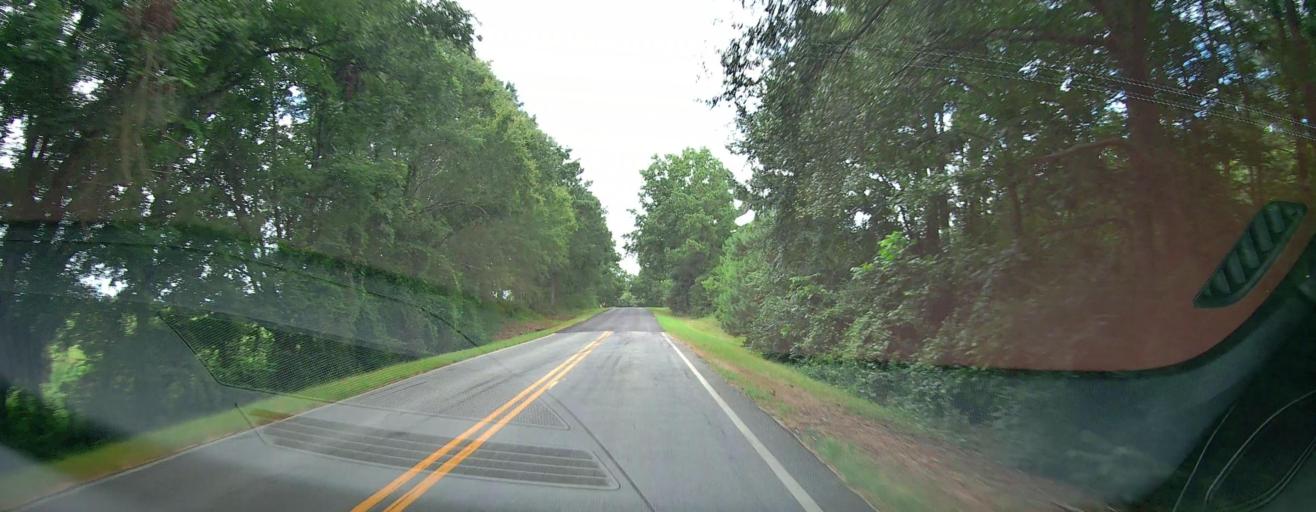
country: US
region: Georgia
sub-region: Dooly County
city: Unadilla
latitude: 32.2914
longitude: -83.8725
